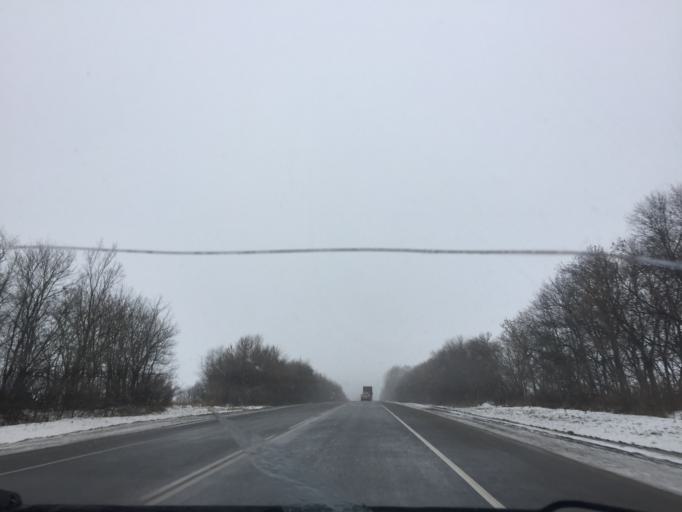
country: RU
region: Tula
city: Plavsk
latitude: 53.7929
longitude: 37.3716
